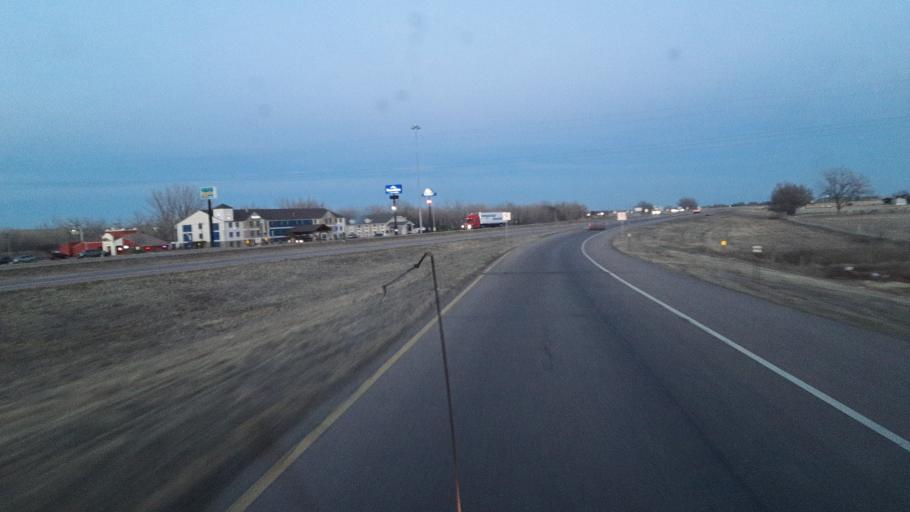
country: US
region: Nebraska
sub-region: Keith County
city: Ogallala
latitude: 41.1146
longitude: -101.7119
